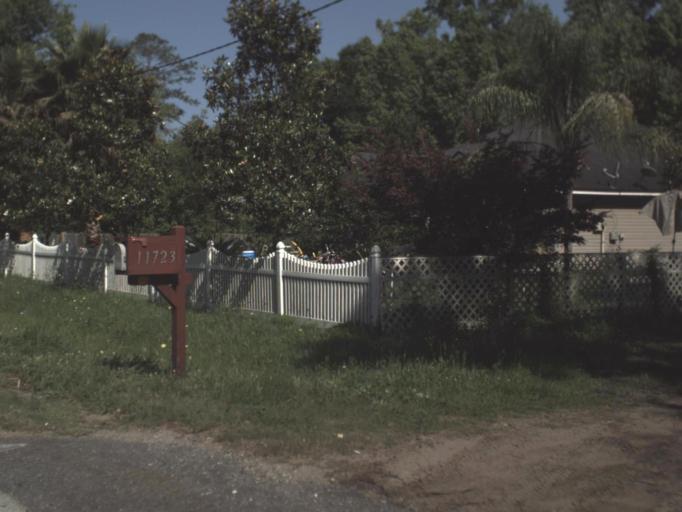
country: US
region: Florida
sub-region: Duval County
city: Baldwin
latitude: 30.3131
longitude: -81.8592
